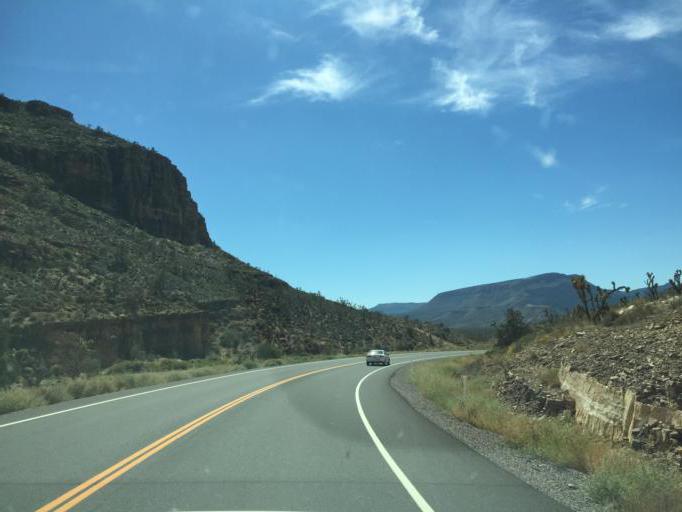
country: US
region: Arizona
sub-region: Mohave County
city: Meadview
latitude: 35.8944
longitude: -113.9470
